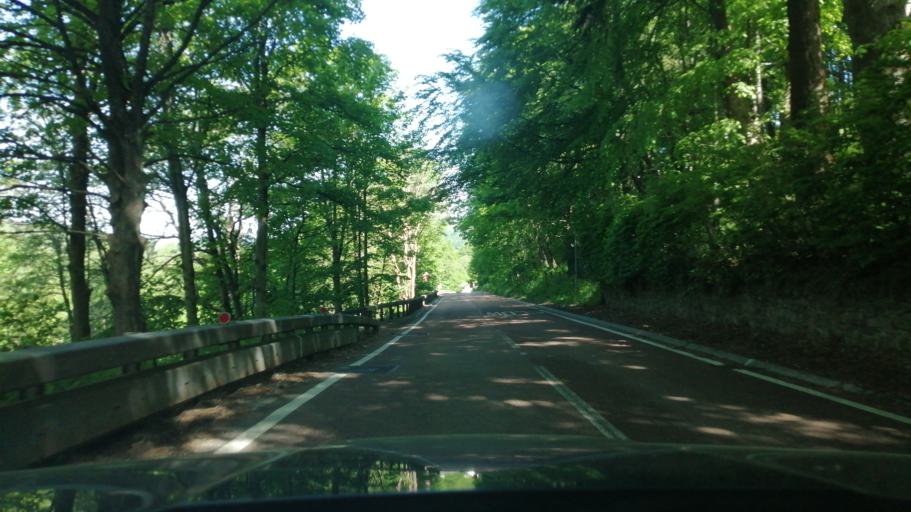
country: GB
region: Scotland
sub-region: Moray
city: Rothes
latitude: 57.4886
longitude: -3.1795
